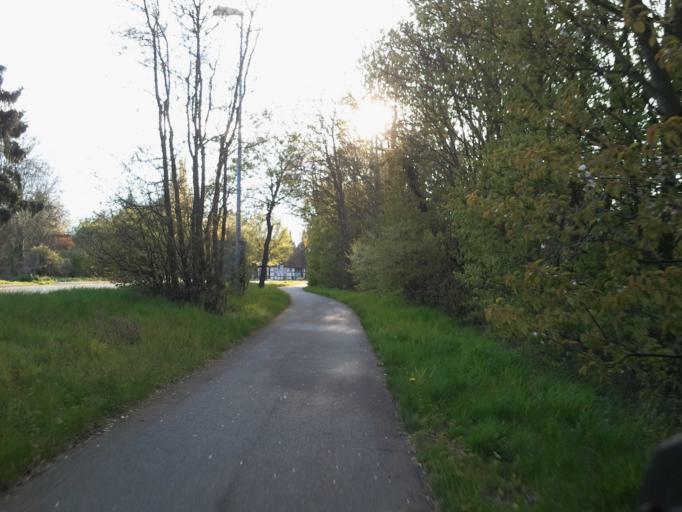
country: DE
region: Lower Saxony
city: Nienburg
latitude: 52.6646
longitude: 9.2535
